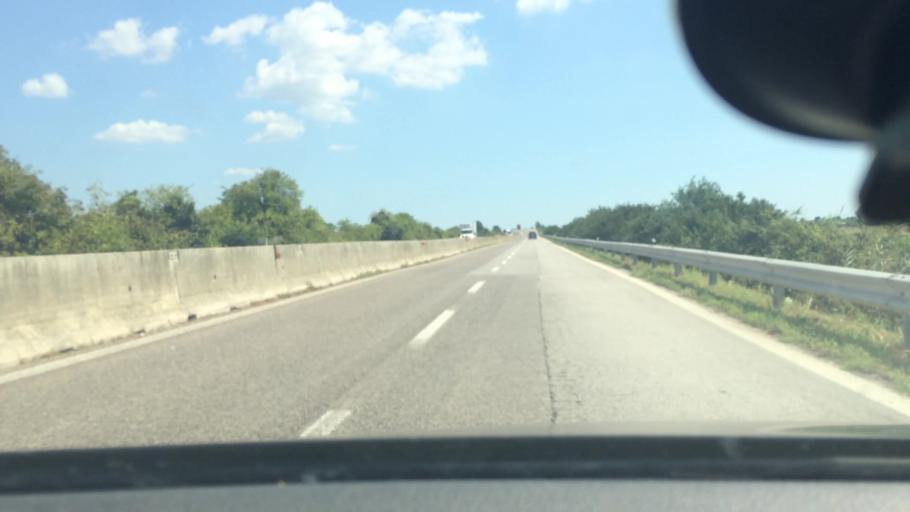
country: IT
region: Emilia-Romagna
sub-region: Provincia di Ferrara
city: Ostellato
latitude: 44.7555
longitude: 11.9455
